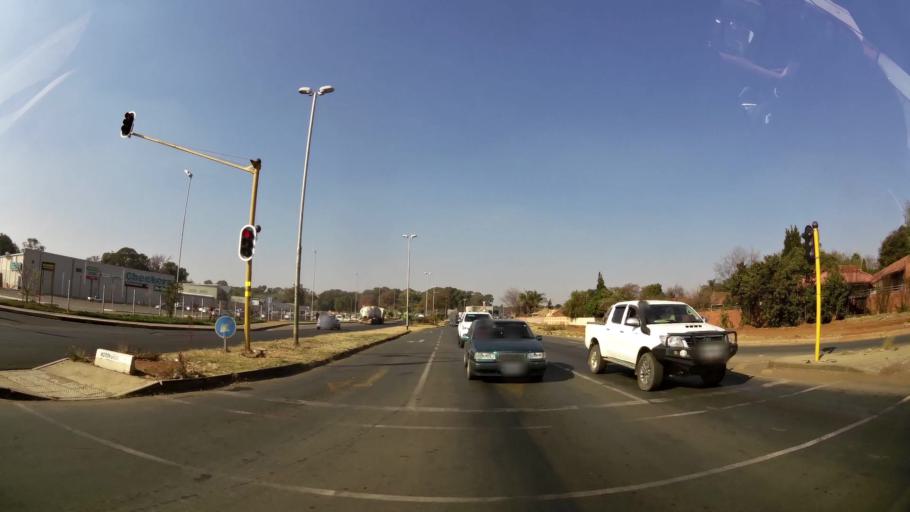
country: ZA
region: Gauteng
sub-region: West Rand District Municipality
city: Randfontein
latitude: -26.1729
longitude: 27.6896
